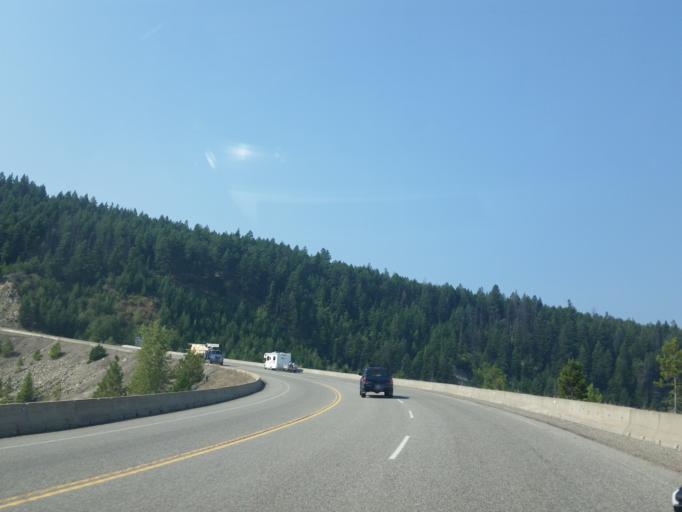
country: CA
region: British Columbia
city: Princeton
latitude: 49.3617
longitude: -120.5673
